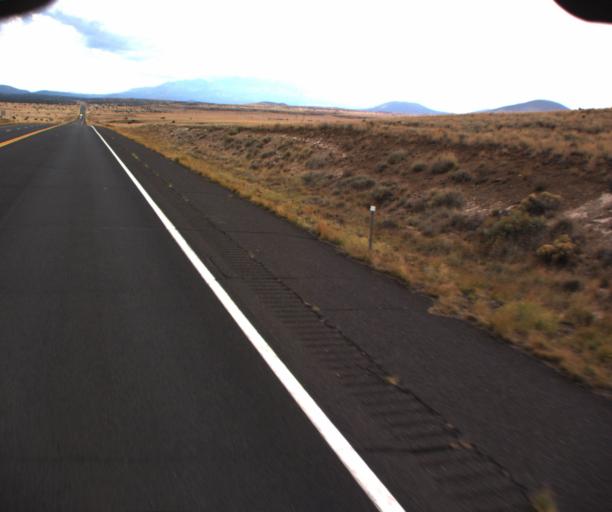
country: US
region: Arizona
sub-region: Coconino County
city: Flagstaff
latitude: 35.5687
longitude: -111.5324
